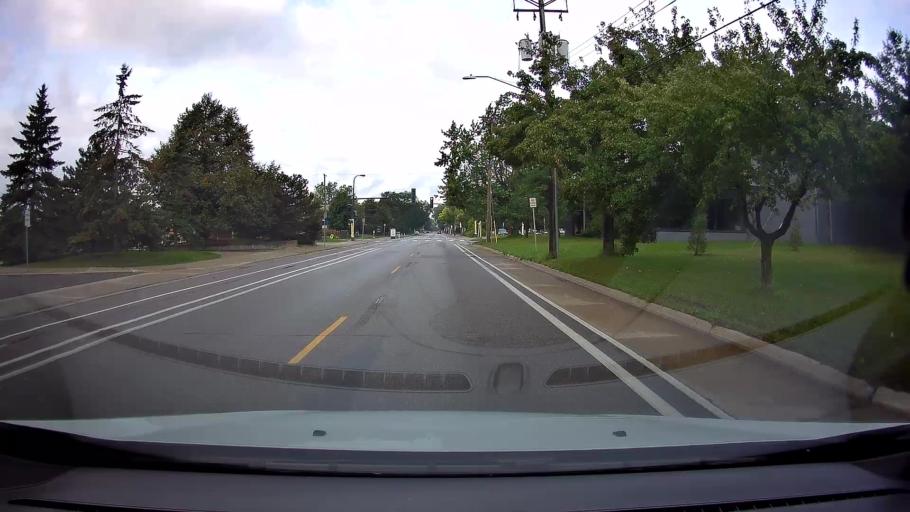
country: US
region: Minnesota
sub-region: Ramsey County
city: Lauderdale
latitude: 44.9880
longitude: -93.2117
